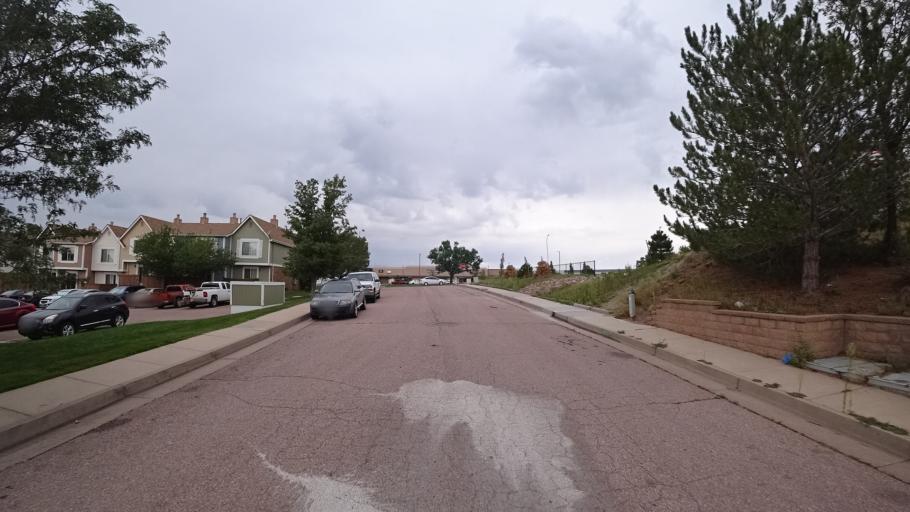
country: US
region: Colorado
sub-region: El Paso County
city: Colorado Springs
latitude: 38.9250
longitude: -104.7952
